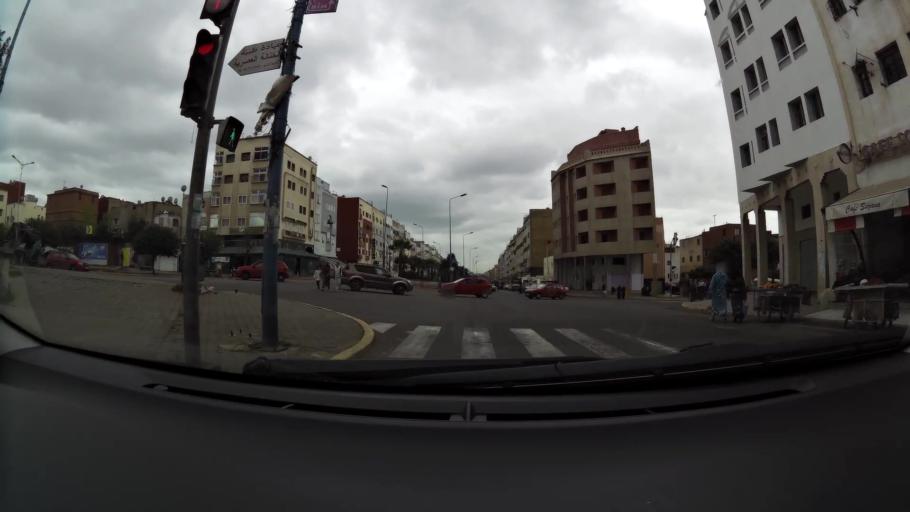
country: MA
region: Grand Casablanca
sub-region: Mediouna
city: Tit Mellil
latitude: 33.5659
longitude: -7.5435
